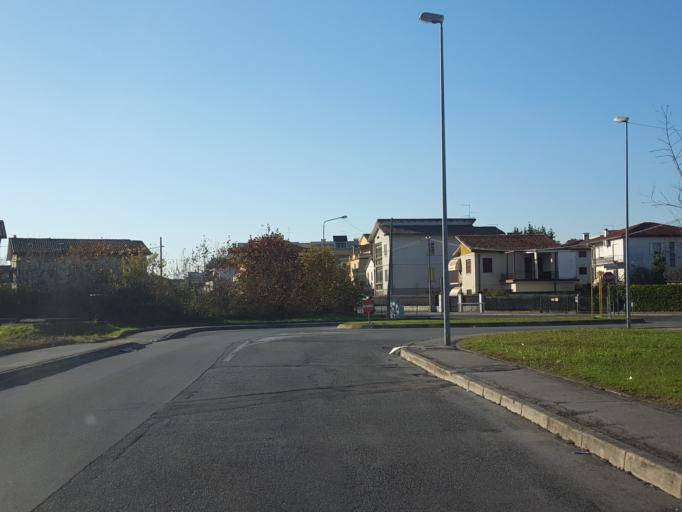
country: IT
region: Veneto
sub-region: Provincia di Vicenza
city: Villaggio Montegrappa
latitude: 45.5402
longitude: 11.5965
